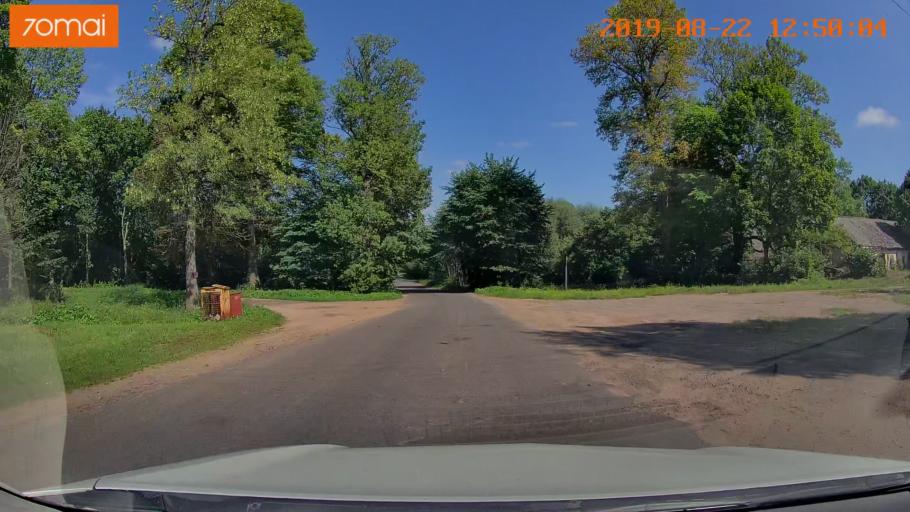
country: BY
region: Minsk
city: Prawdzinski
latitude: 53.4581
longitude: 27.6406
